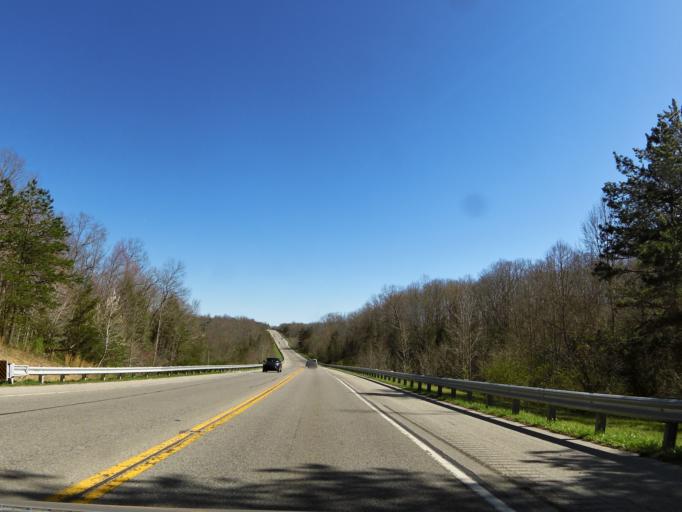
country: US
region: Kentucky
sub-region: McCreary County
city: Stearns
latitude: 36.6860
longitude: -84.4524
